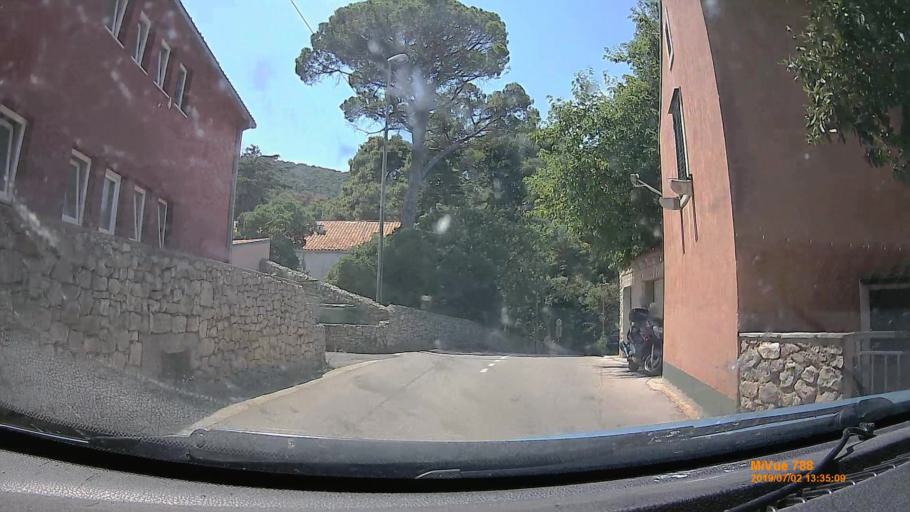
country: HR
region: Primorsko-Goranska
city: Mali Losinj
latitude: 44.5178
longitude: 14.5018
